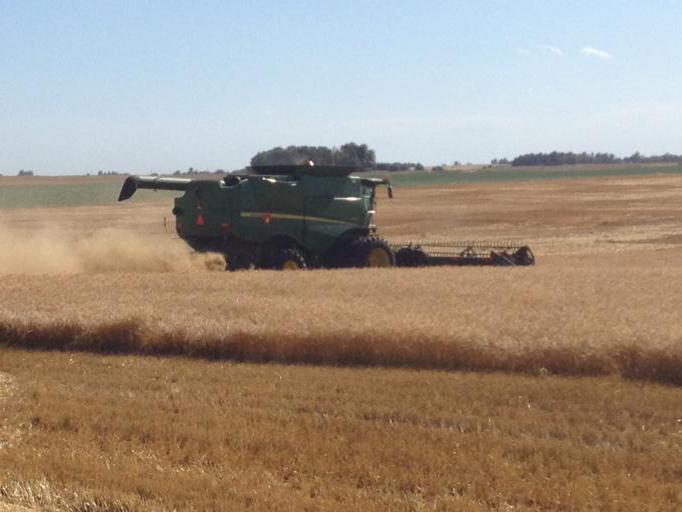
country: US
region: Kansas
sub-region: Rice County
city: Lyons
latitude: 38.3172
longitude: -98.3588
